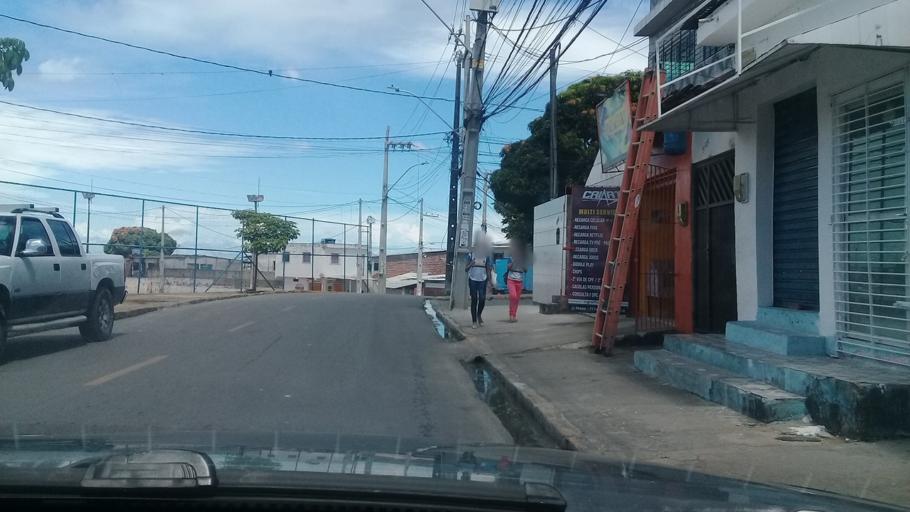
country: BR
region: Pernambuco
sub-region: Jaboatao Dos Guararapes
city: Jaboatao dos Guararapes
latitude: -8.1203
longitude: -34.9459
